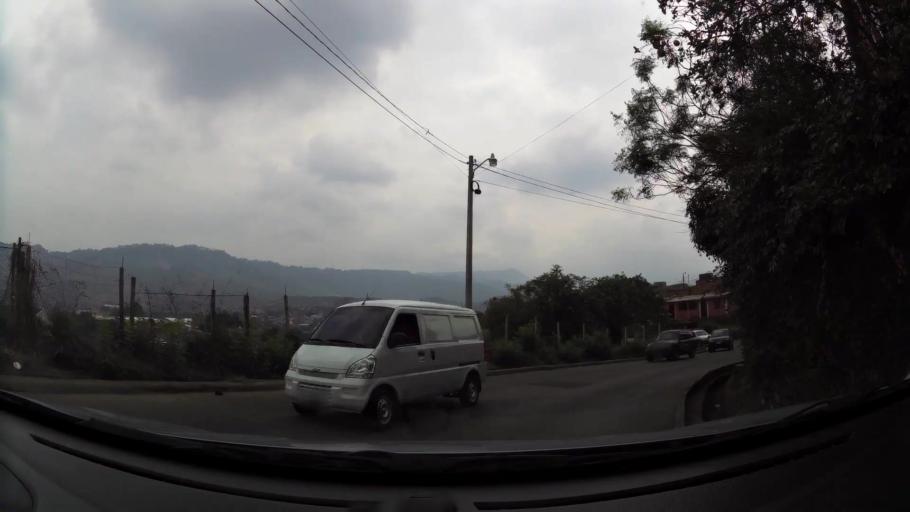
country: HN
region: Francisco Morazan
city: Tegucigalpa
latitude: 14.0988
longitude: -87.1751
